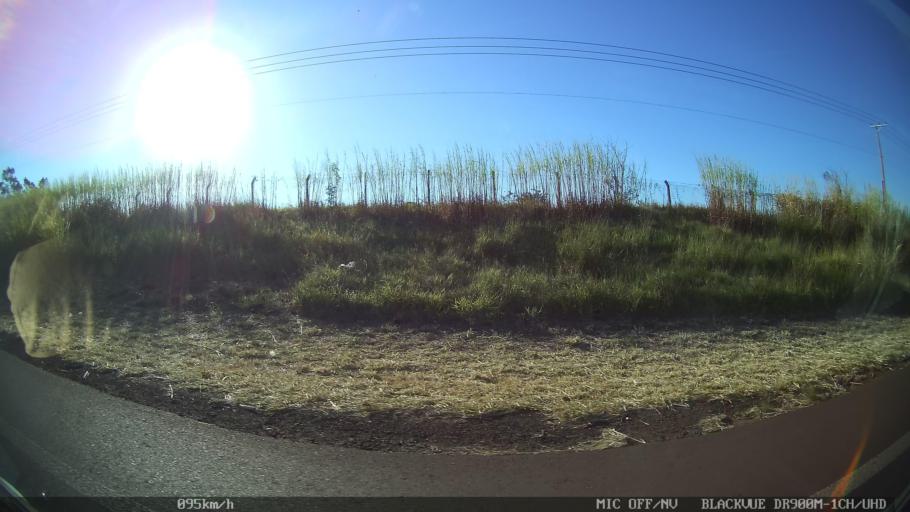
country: BR
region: Sao Paulo
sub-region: Olimpia
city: Olimpia
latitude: -20.7088
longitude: -48.9686
